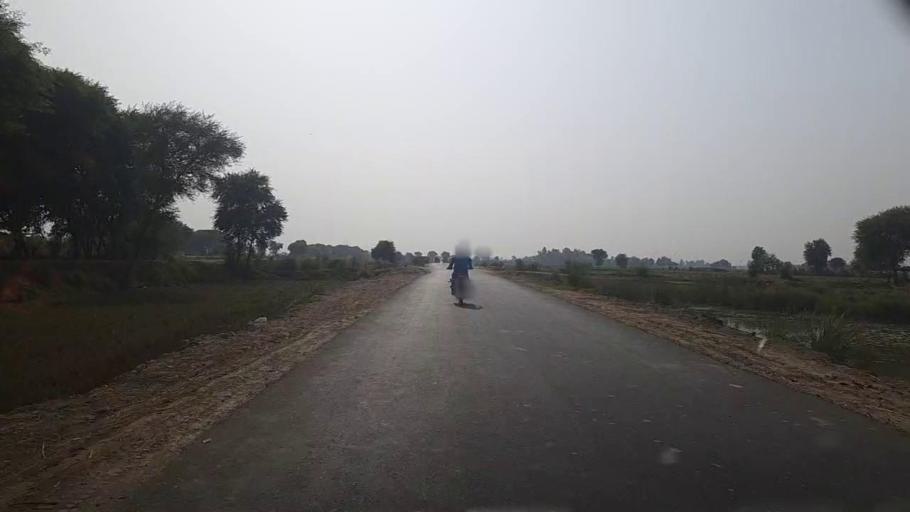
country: PK
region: Sindh
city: Kashmor
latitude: 28.4058
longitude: 69.5574
